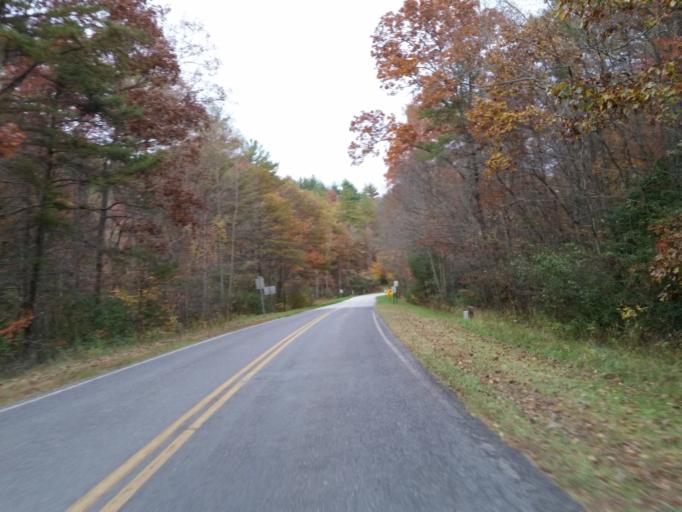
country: US
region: Georgia
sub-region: Fannin County
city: Blue Ridge
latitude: 34.6935
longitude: -84.2528
